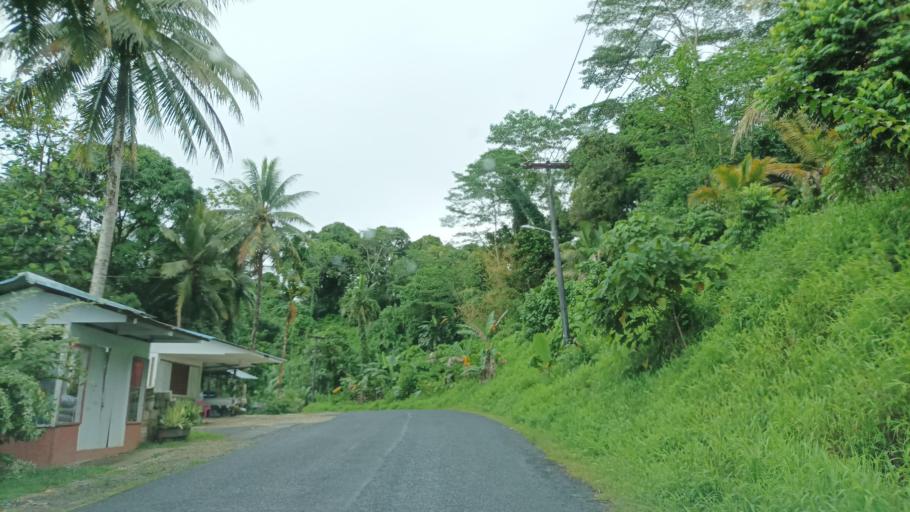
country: FM
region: Pohnpei
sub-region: Sokehs Municipality
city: Palikir - National Government Center
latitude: 6.8846
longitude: 158.1574
